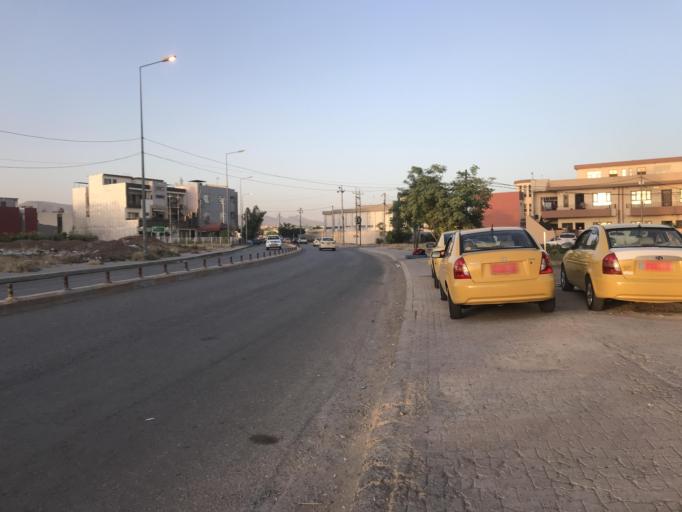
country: IQ
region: Dahuk
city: Saymayl
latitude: 36.8591
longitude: 42.8330
